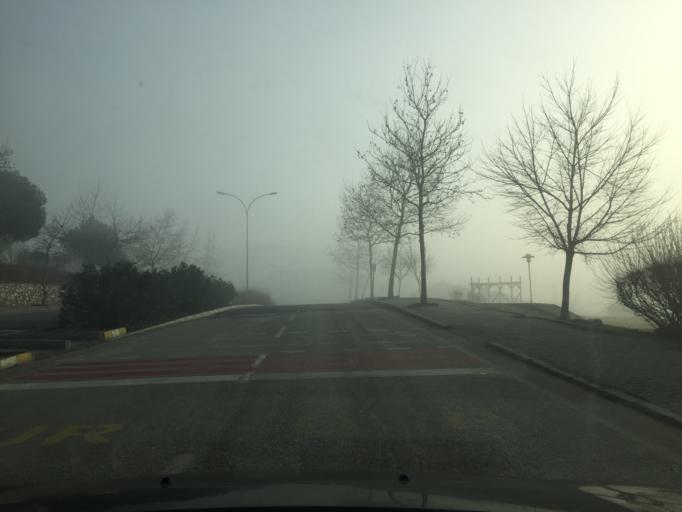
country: TR
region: Duzce
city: Duzce
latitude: 40.8677
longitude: 31.2201
